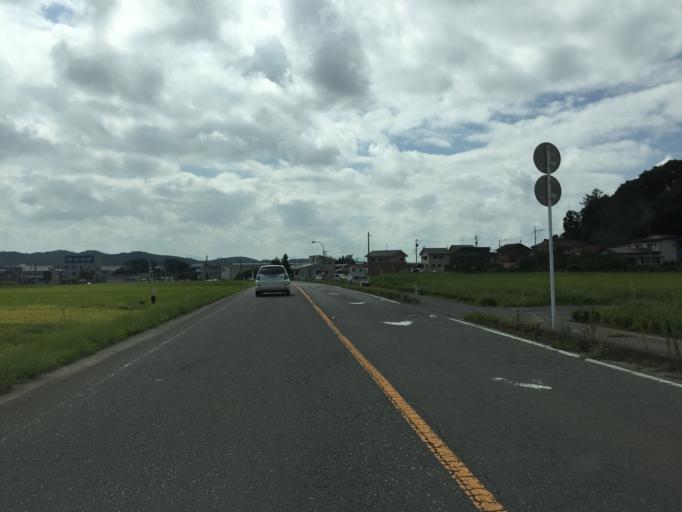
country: JP
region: Fukushima
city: Motomiya
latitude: 37.4897
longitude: 140.3712
